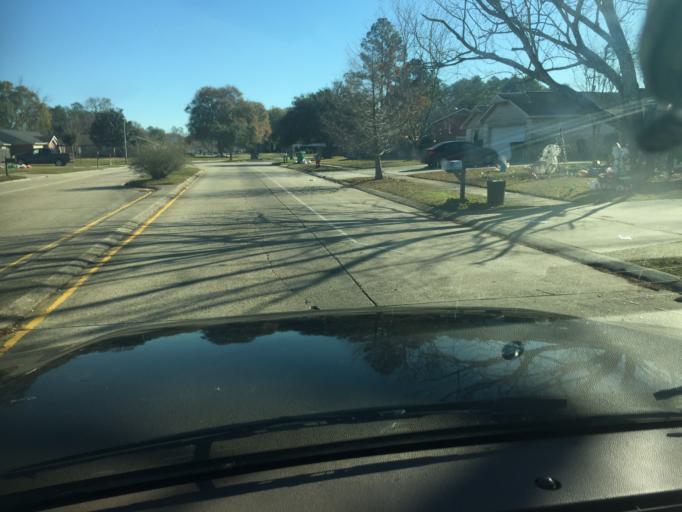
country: US
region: Louisiana
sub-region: Saint Tammany Parish
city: Slidell
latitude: 30.2997
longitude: -89.7632
